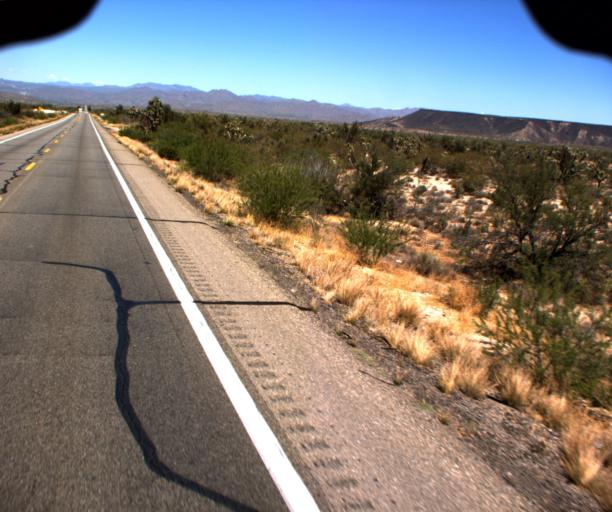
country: US
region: Arizona
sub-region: Yavapai County
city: Congress
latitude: 34.2918
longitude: -113.1115
